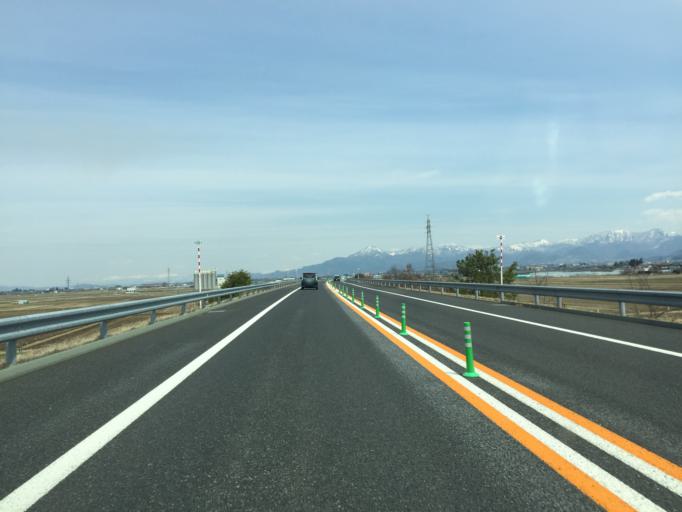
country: JP
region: Yamagata
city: Tendo
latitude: 38.3483
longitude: 140.3367
